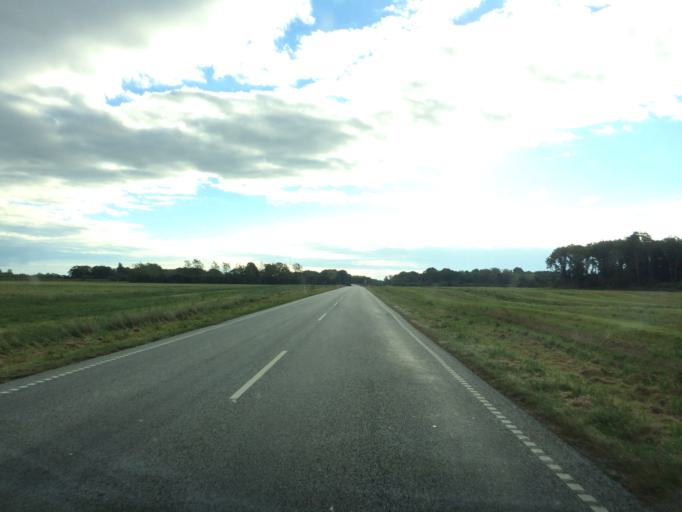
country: DK
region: Central Jutland
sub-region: Herning Kommune
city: Kibaek
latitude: 55.9465
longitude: 8.7611
